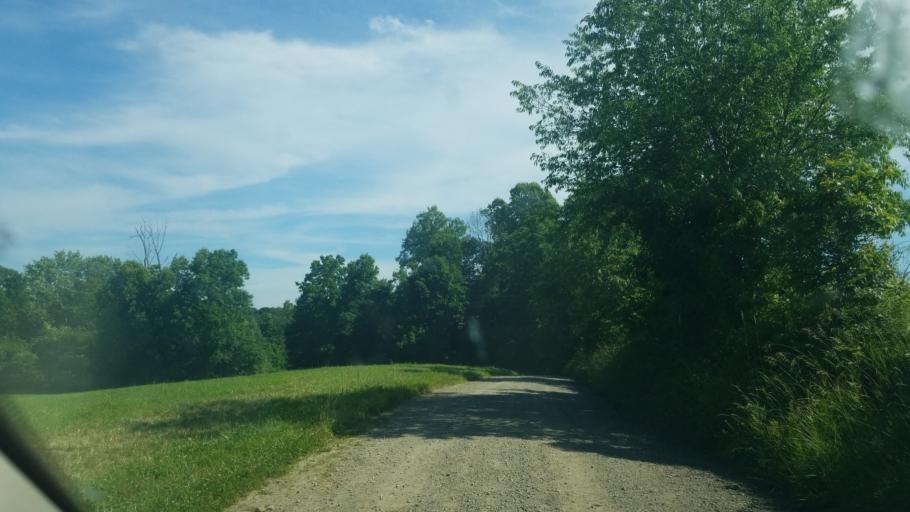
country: US
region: Ohio
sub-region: Holmes County
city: Millersburg
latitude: 40.4559
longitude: -81.9558
